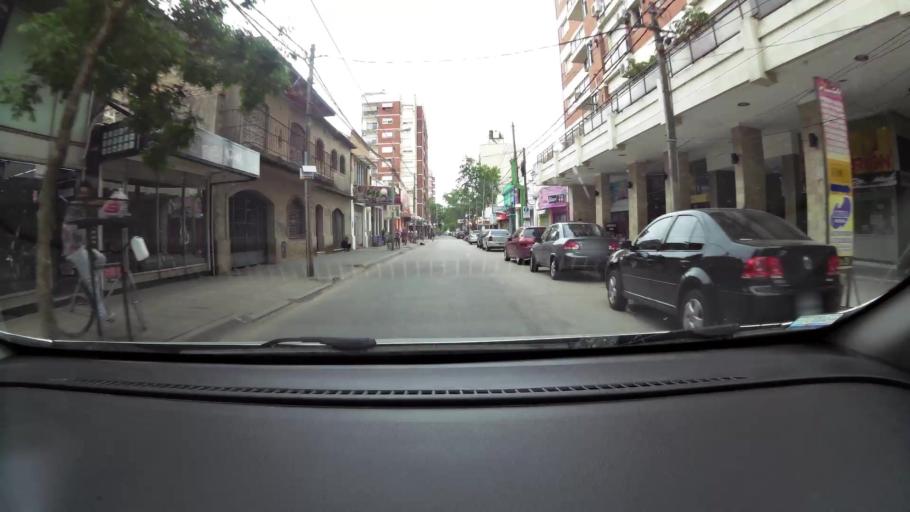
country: AR
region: Buenos Aires
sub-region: Partido de Zarate
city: Zarate
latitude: -34.0991
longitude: -59.0234
